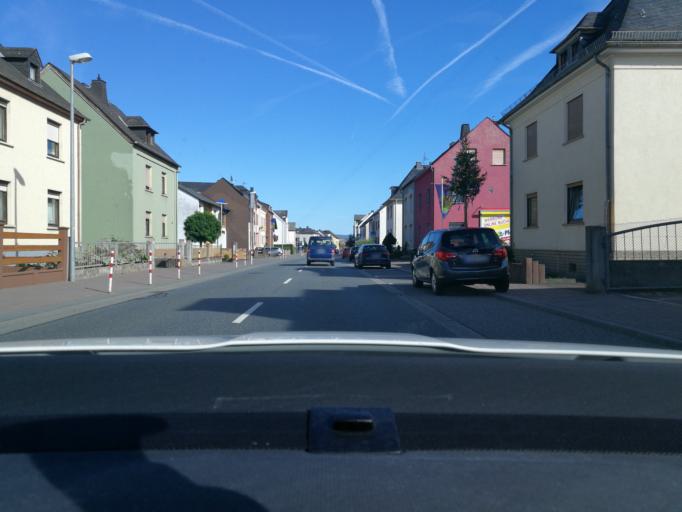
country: DE
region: Hesse
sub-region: Regierungsbezirk Giessen
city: Steeden
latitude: 50.3739
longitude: 8.1168
